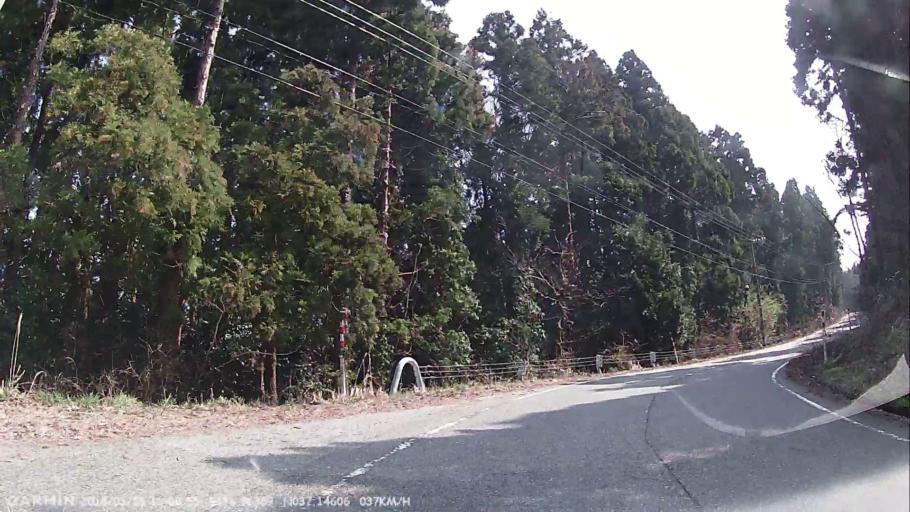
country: JP
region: Ishikawa
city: Nanao
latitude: 37.1461
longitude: 136.9639
